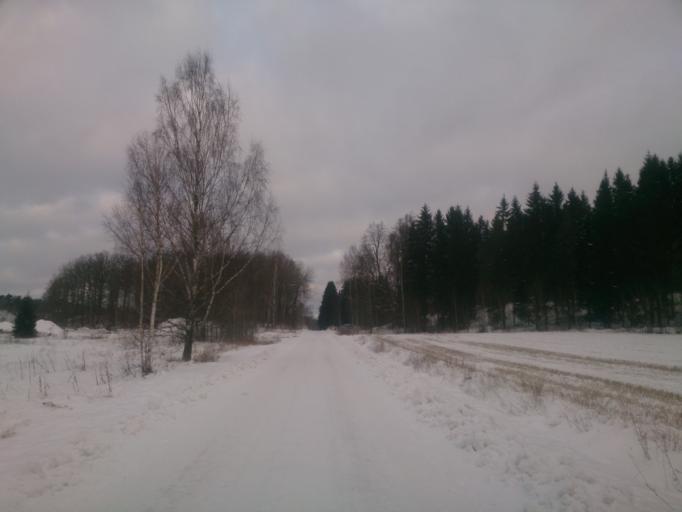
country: SE
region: OEstergoetland
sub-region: Atvidabergs Kommun
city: Atvidaberg
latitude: 58.2169
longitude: 15.9894
